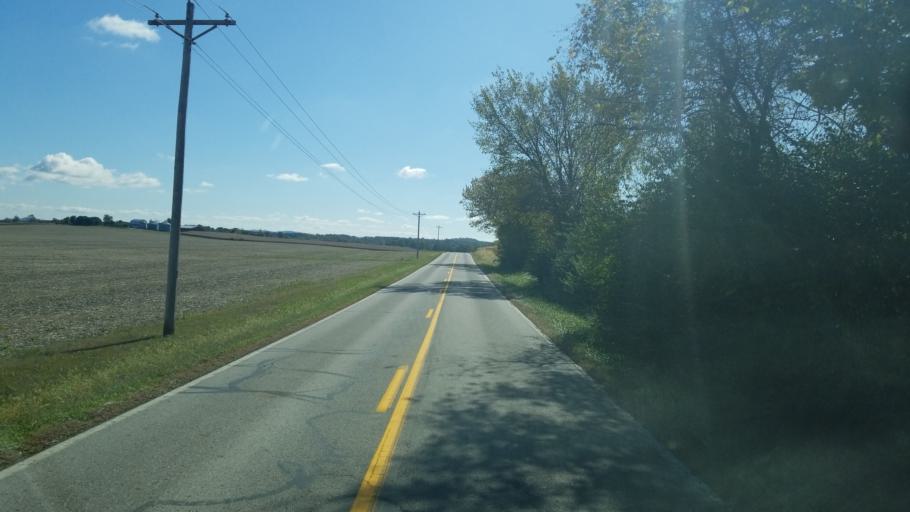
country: US
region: Ohio
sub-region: Highland County
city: Leesburg
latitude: 39.2850
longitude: -83.5005
